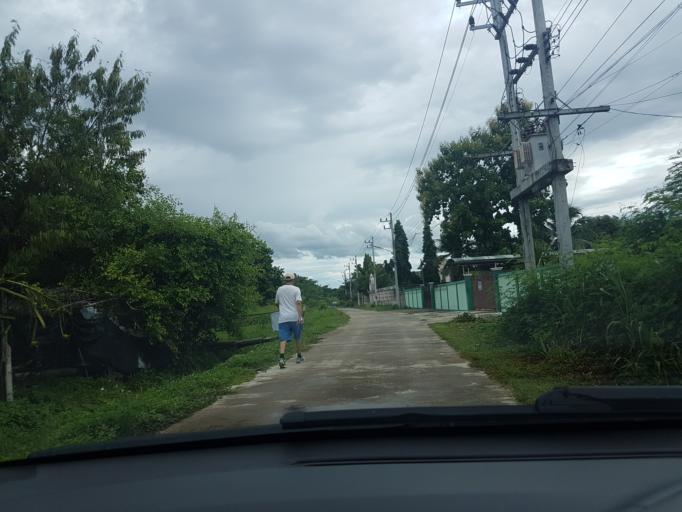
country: TH
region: Lampang
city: Lampang
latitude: 18.3124
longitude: 99.4797
